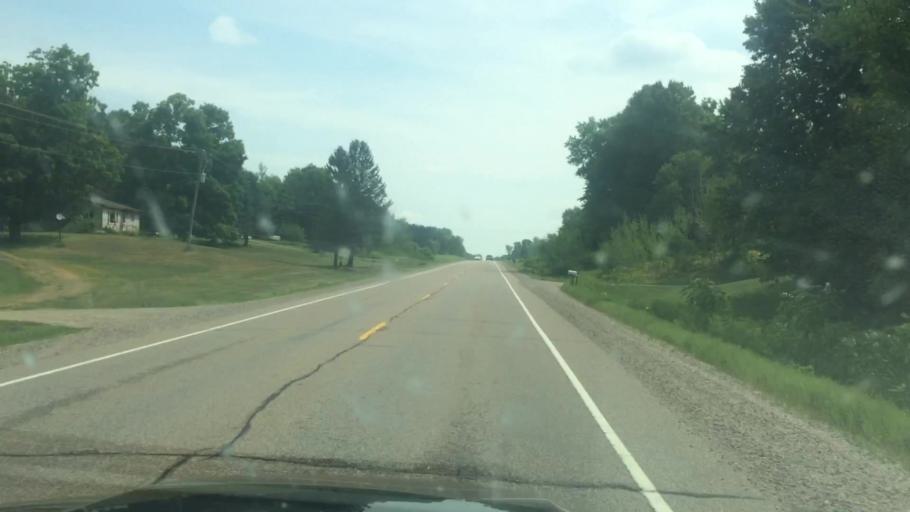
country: US
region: Wisconsin
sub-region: Langlade County
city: Antigo
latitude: 45.1685
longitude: -88.9534
